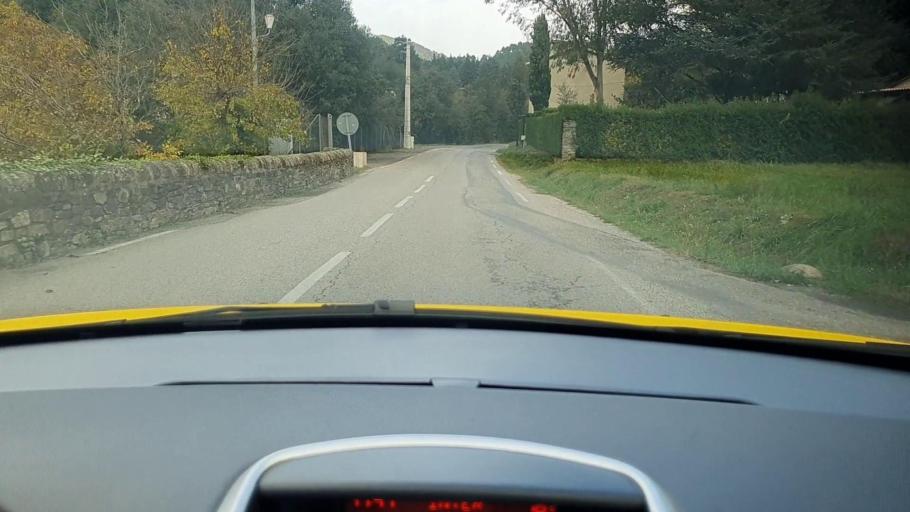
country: FR
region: Languedoc-Roussillon
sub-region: Departement du Gard
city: Lasalle
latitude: 44.1200
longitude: 3.7619
